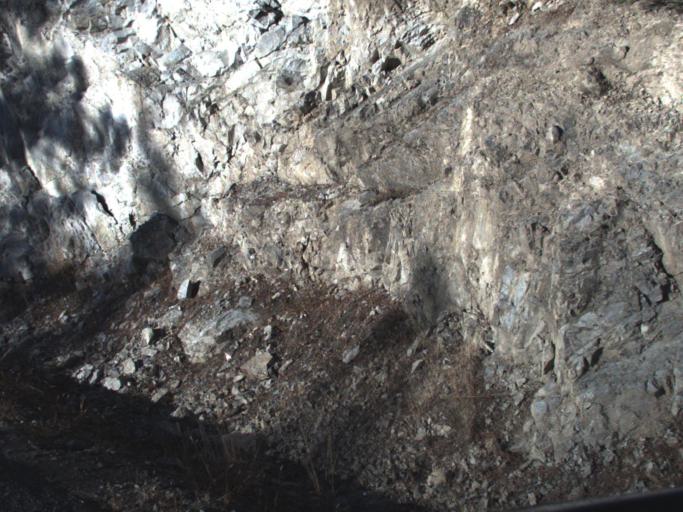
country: US
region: Washington
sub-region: Okanogan County
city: Coulee Dam
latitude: 48.0234
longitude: -118.6717
